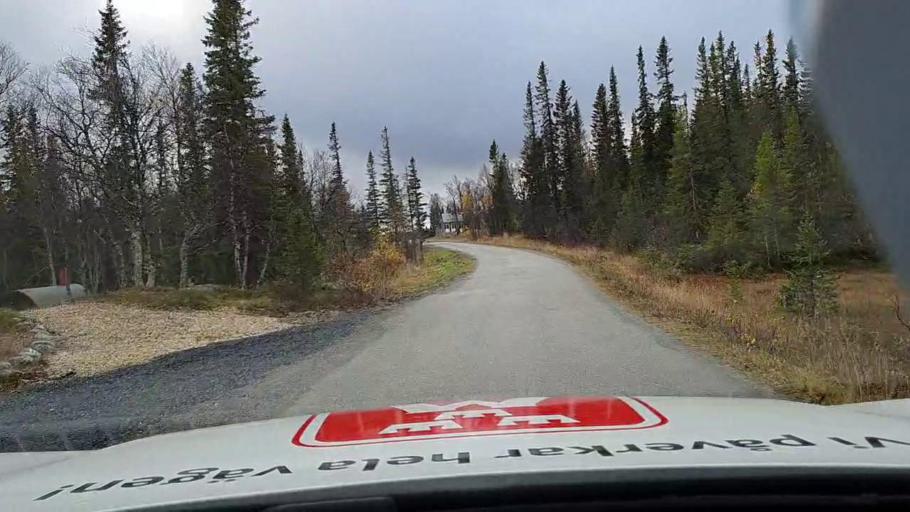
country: SE
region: Jaemtland
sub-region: Krokoms Kommun
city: Valla
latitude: 63.0261
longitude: 13.9402
